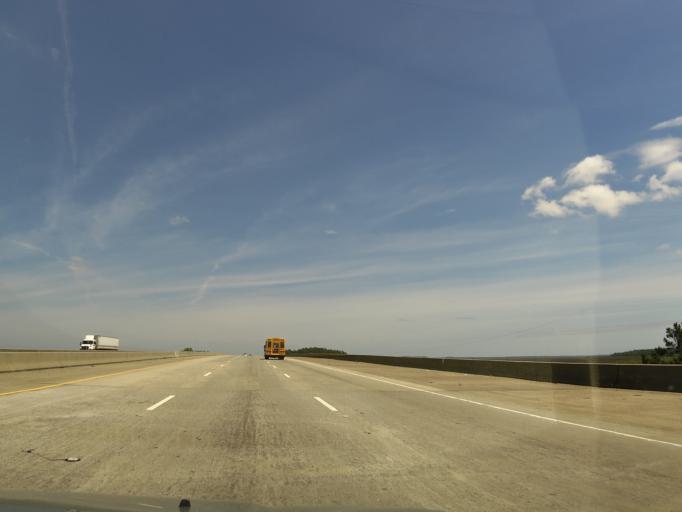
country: US
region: Georgia
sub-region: Camden County
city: Woodbine
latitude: 30.9537
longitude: -81.6834
